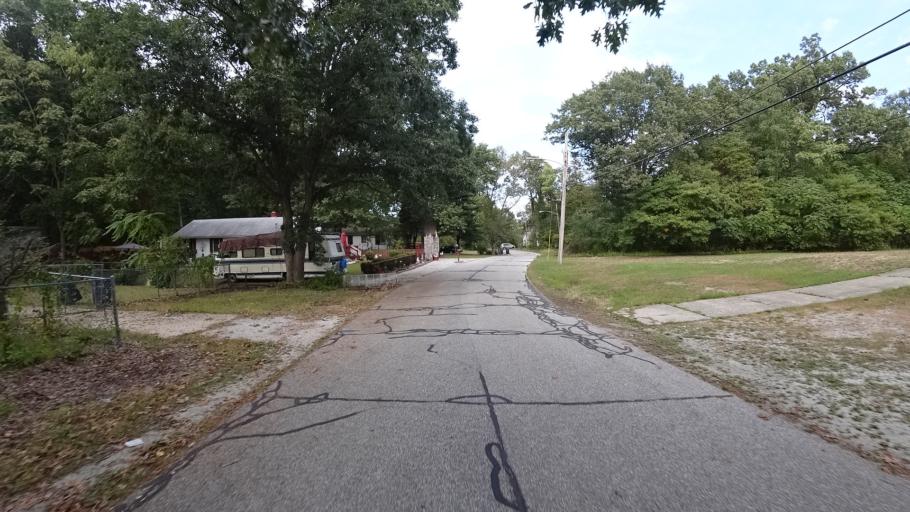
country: US
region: Indiana
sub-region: LaPorte County
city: Long Beach
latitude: 41.7287
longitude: -86.8598
